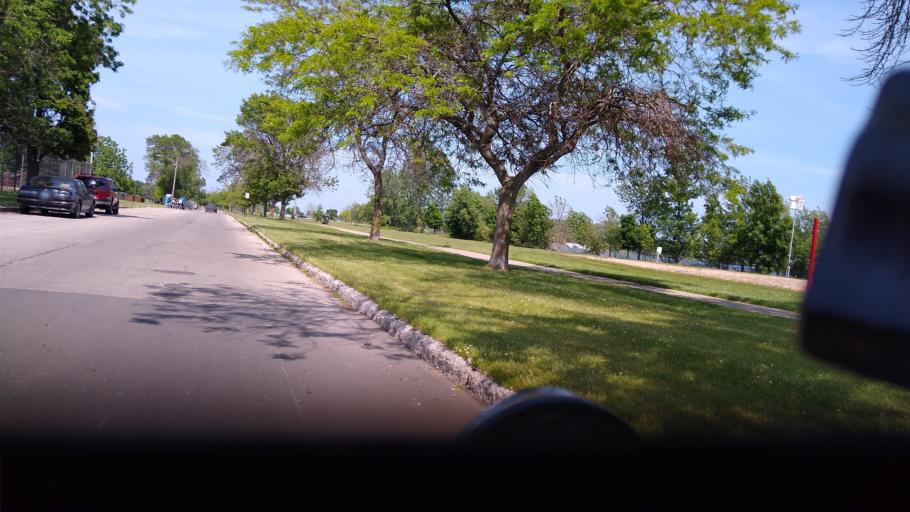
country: US
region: Michigan
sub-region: Delta County
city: Escanaba
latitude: 45.7387
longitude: -87.0544
